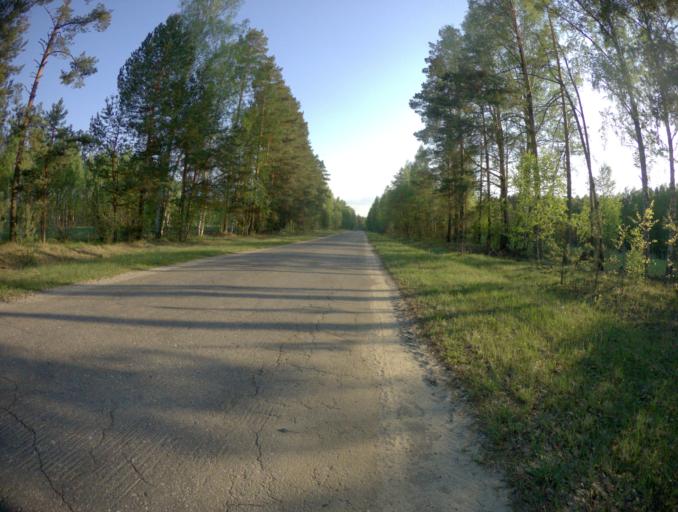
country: RU
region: Vladimir
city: Vyazniki
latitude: 56.3393
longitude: 42.1364
